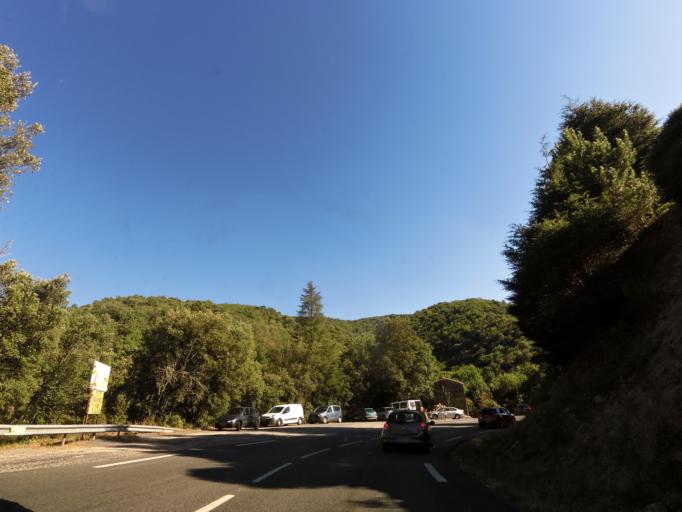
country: FR
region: Languedoc-Roussillon
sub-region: Departement du Gard
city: Valleraugue
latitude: 44.0459
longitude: 3.6865
